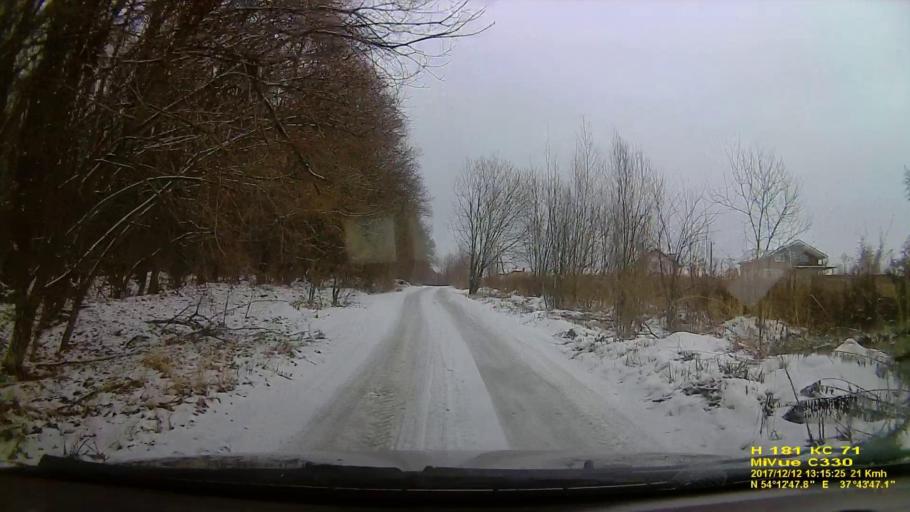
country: RU
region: Tula
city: Tula
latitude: 54.2133
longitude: 37.7298
